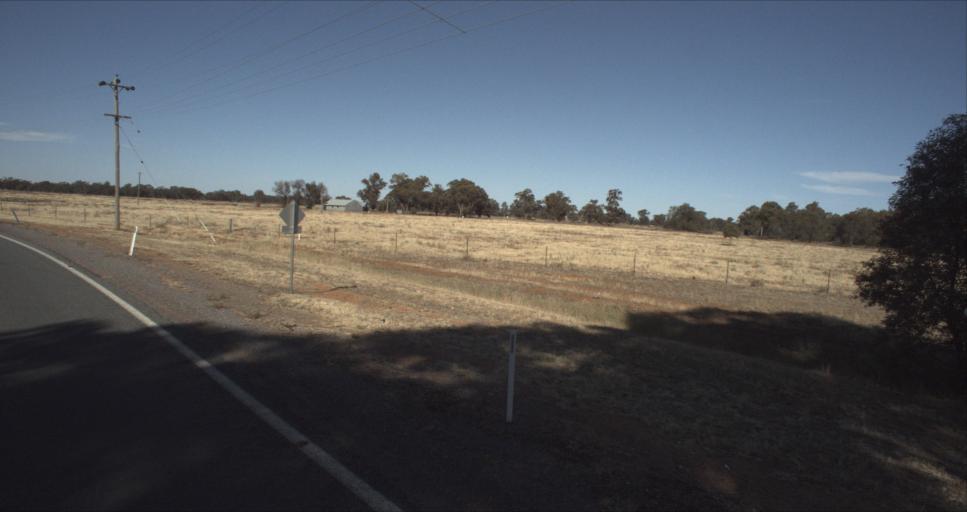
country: AU
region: New South Wales
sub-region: Leeton
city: Leeton
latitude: -34.6254
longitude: 146.3941
